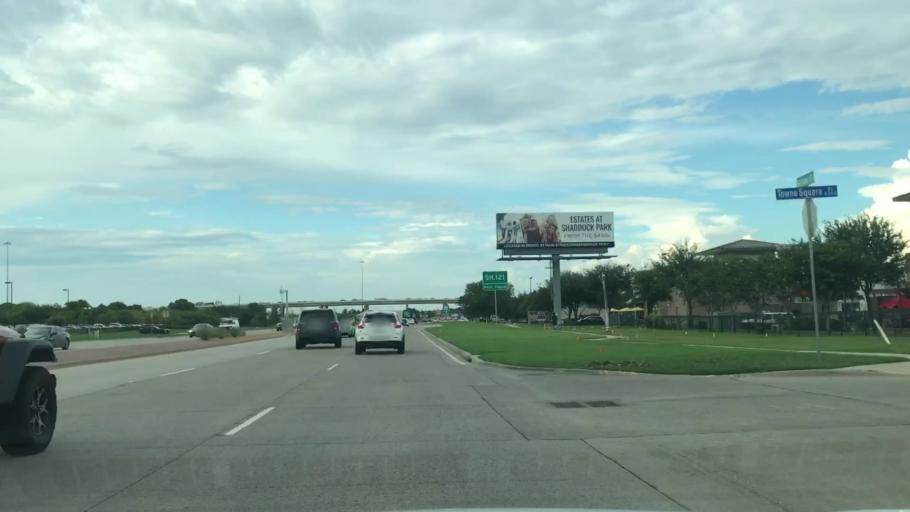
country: US
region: Texas
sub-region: Collin County
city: Frisco
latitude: 33.0911
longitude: -96.8054
